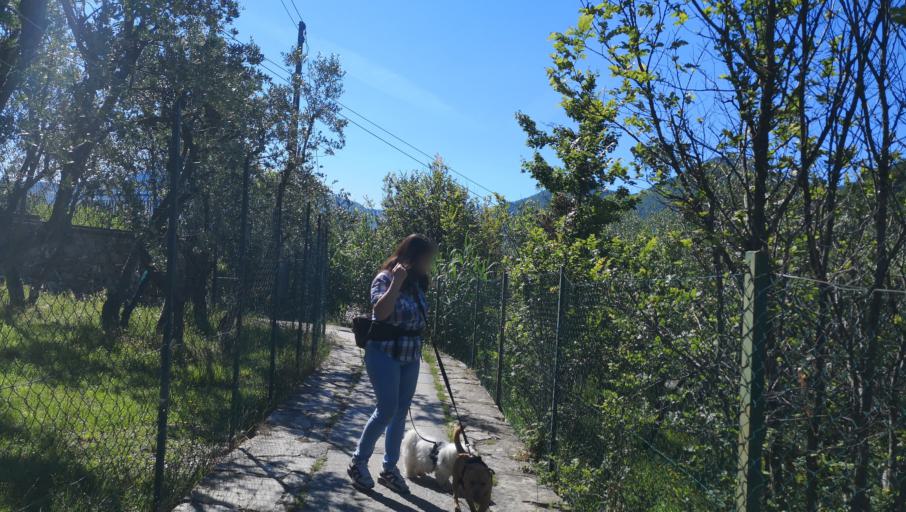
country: IT
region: Liguria
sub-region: Provincia di Genova
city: Piccarello
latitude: 44.4556
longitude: 8.9877
